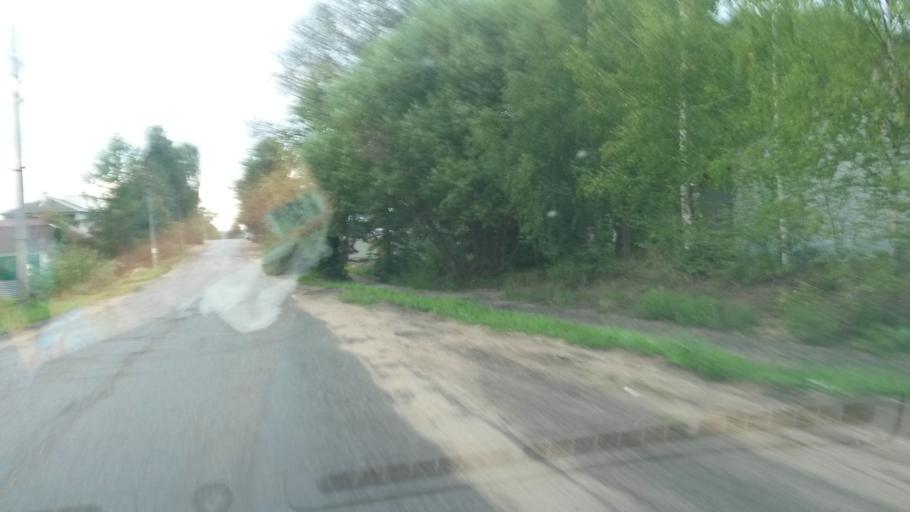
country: RU
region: Jaroslavl
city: Petrovsk
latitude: 57.0106
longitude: 39.2663
